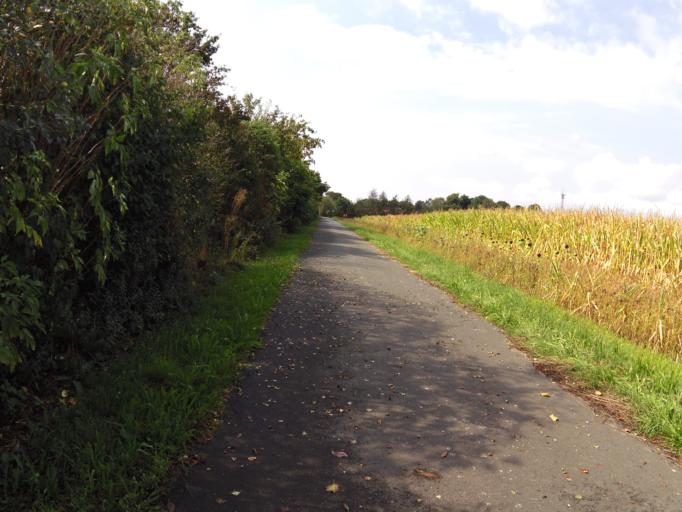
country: DE
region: Lower Saxony
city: Bucken
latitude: 52.7816
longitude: 9.1407
